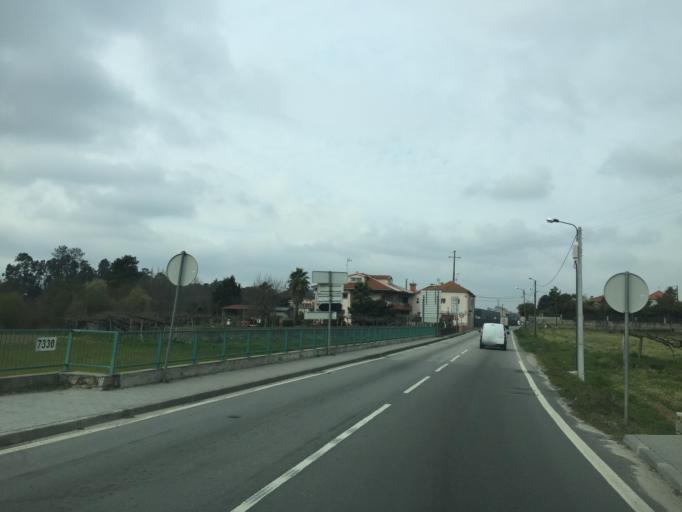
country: PT
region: Porto
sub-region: Paredes
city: Paredes
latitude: 41.1674
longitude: -8.3053
